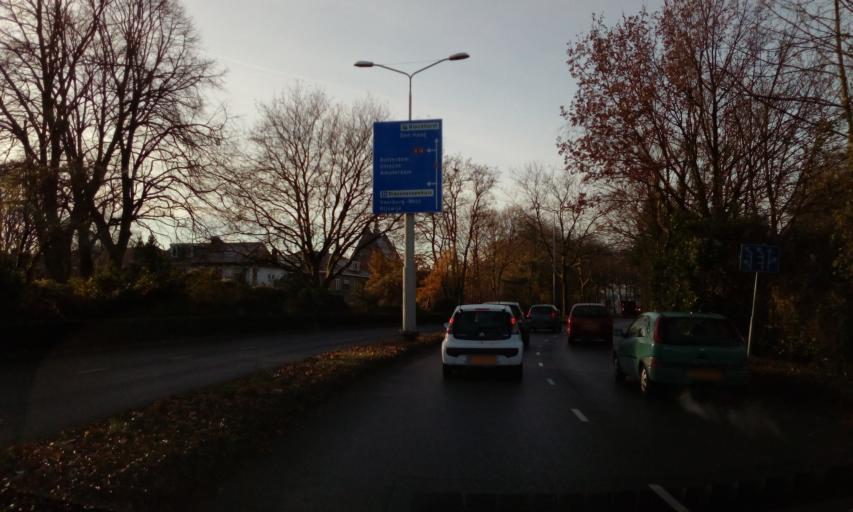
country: NL
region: South Holland
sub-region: Gemeente Leidschendam-Voorburg
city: Voorburg
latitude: 52.0702
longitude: 4.3596
